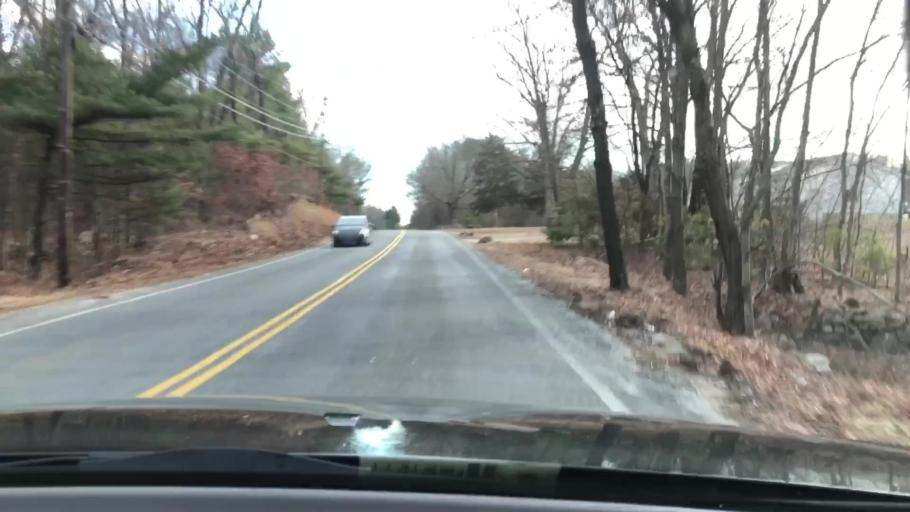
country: US
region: Massachusetts
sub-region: Worcester County
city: Mendon
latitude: 42.0742
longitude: -71.5253
